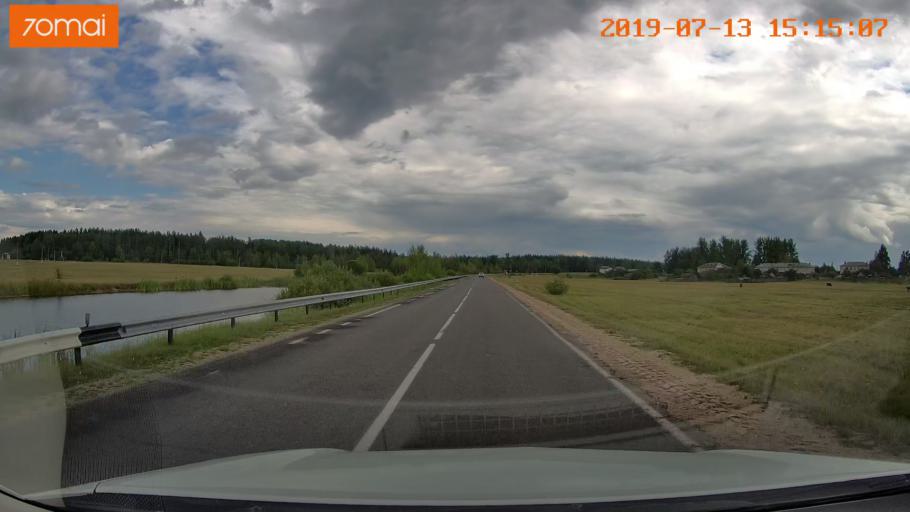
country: BY
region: Mogilev
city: Hlusha
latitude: 53.1191
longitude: 28.8222
